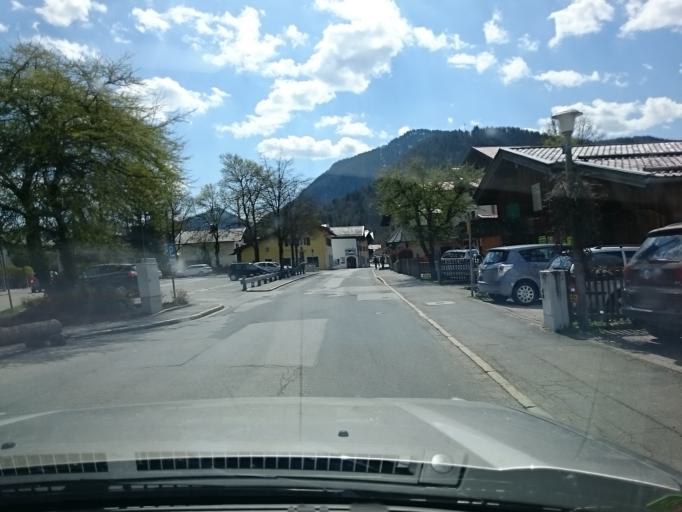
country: DE
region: Bavaria
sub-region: Upper Bavaria
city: Mittenwald
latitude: 47.4400
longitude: 11.2614
